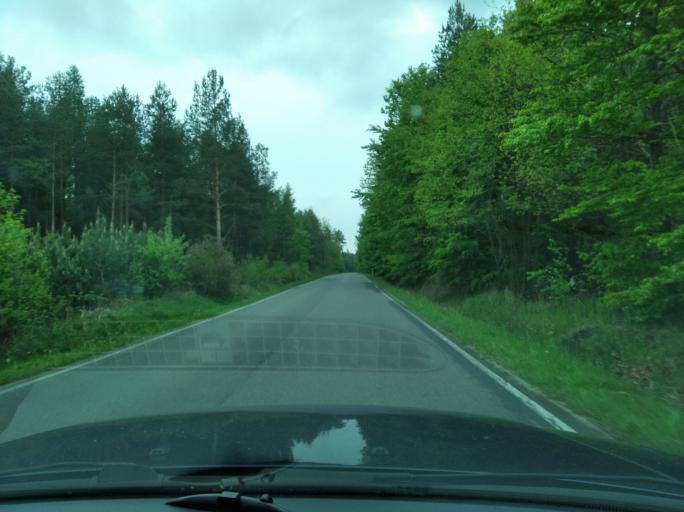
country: PL
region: Subcarpathian Voivodeship
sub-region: Powiat kolbuszowski
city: Kolbuszowa
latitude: 50.1729
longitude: 21.7595
